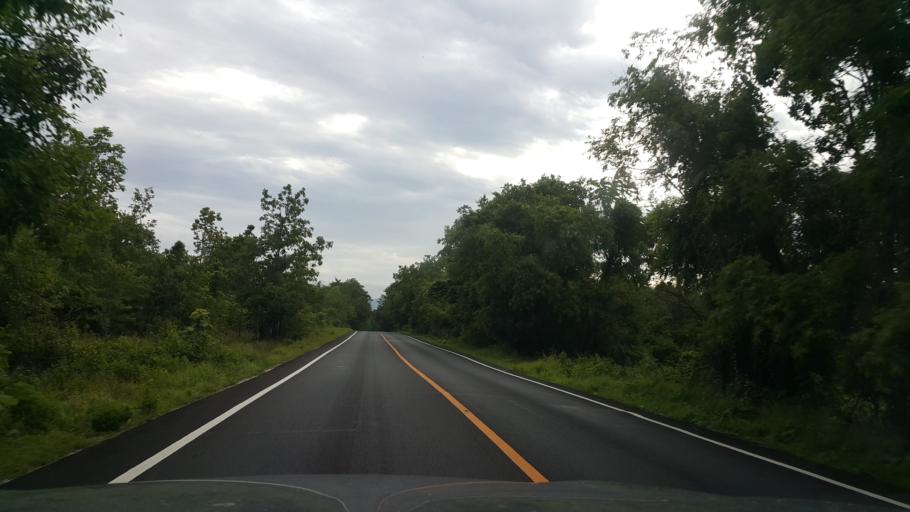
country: TH
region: Lampang
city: Thoen
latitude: 17.6301
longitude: 99.2635
